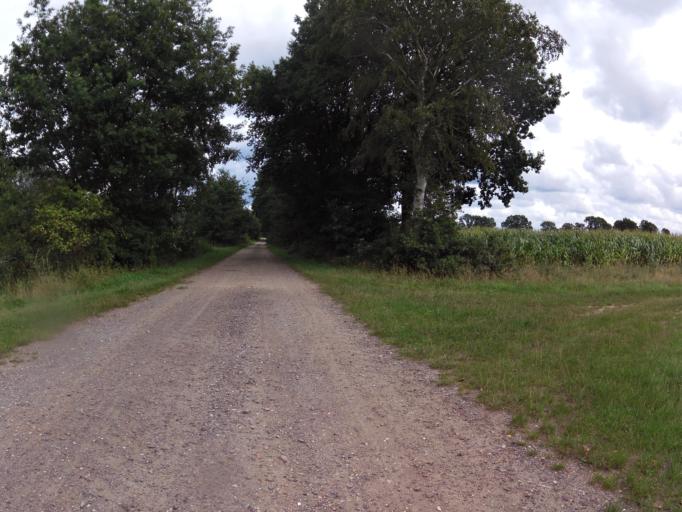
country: DE
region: Lower Saxony
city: Oerel
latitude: 53.4929
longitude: 9.0576
